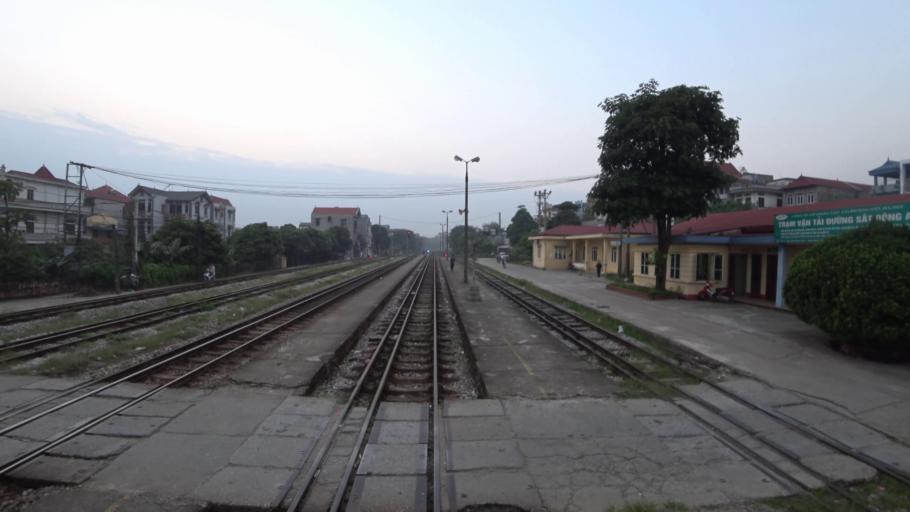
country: VN
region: Ha Noi
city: Dong Anh
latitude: 21.1932
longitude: 105.8549
